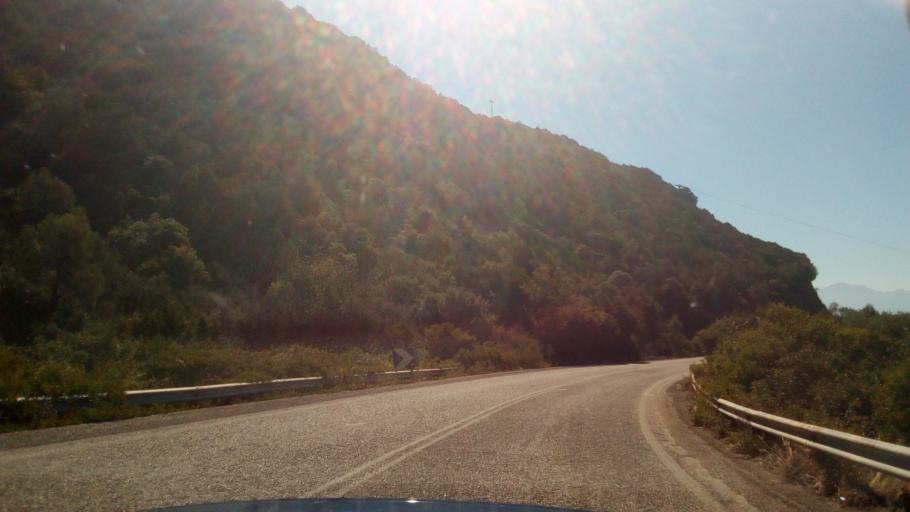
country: GR
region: West Greece
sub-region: Nomos Achaias
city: Selianitika
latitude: 38.3751
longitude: 22.0979
